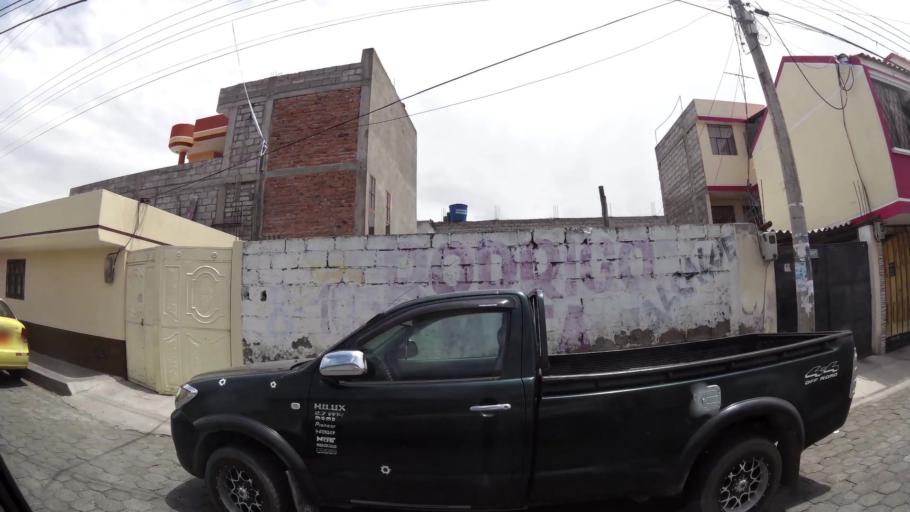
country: EC
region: Cotopaxi
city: San Miguel de Salcedo
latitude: -1.0445
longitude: -78.5934
